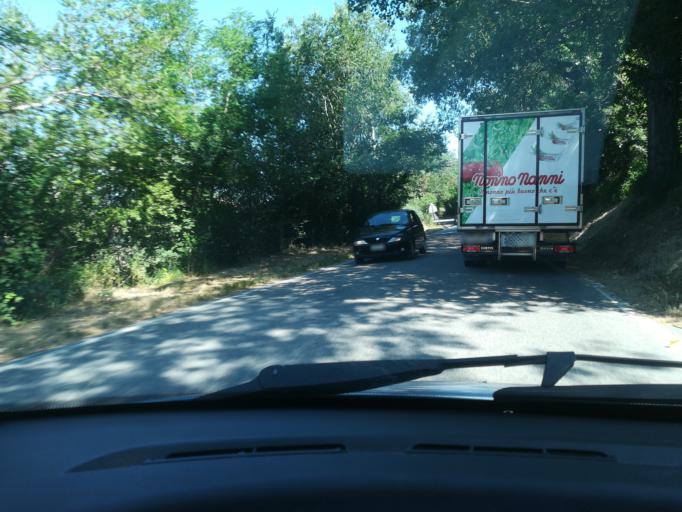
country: IT
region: The Marches
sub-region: Provincia di Macerata
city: San Ginesio
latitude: 43.1116
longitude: 13.3468
